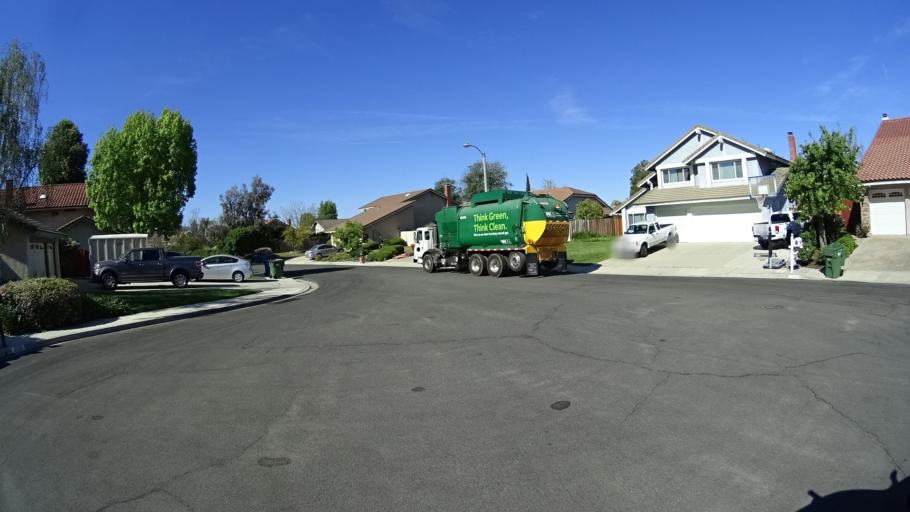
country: US
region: California
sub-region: Ventura County
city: Thousand Oaks
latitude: 34.2280
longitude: -118.8575
